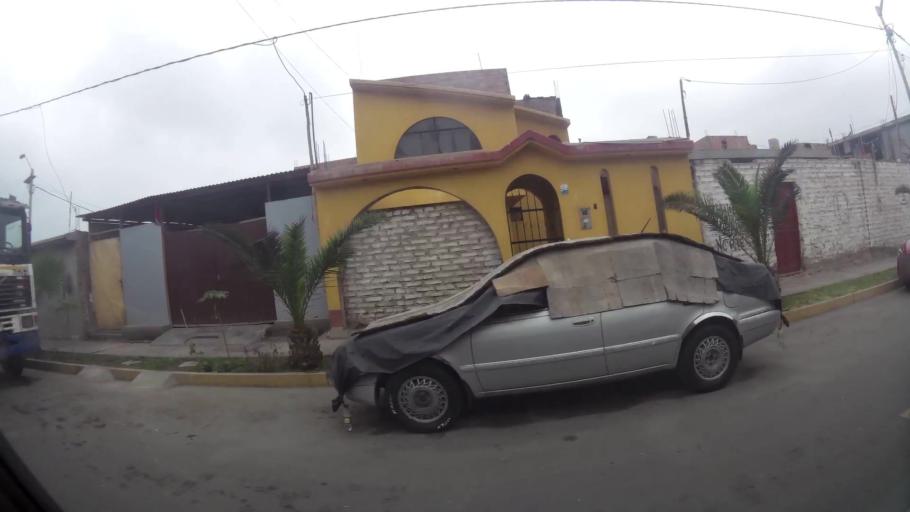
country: PE
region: Lima
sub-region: Provincia de Huaral
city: Chancay
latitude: -11.5604
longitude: -77.2732
